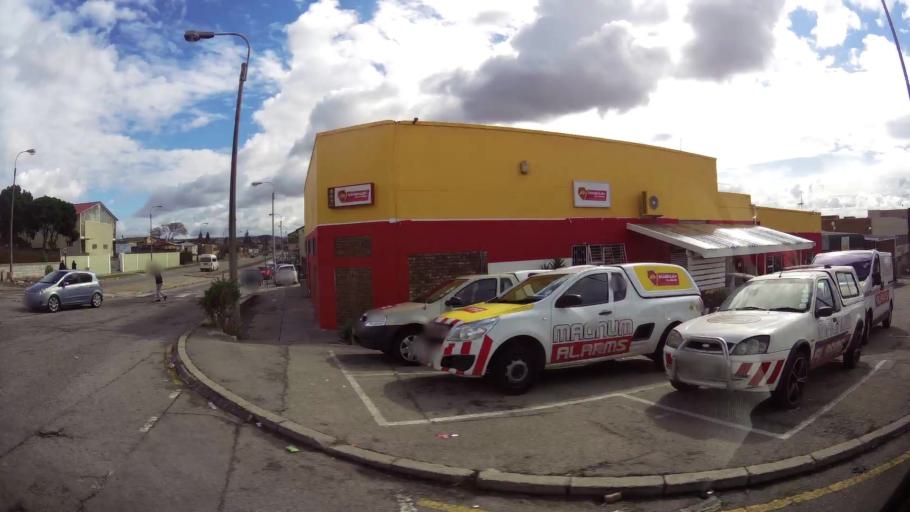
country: ZA
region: Eastern Cape
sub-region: Nelson Mandela Bay Metropolitan Municipality
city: Port Elizabeth
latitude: -33.9290
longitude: 25.5694
